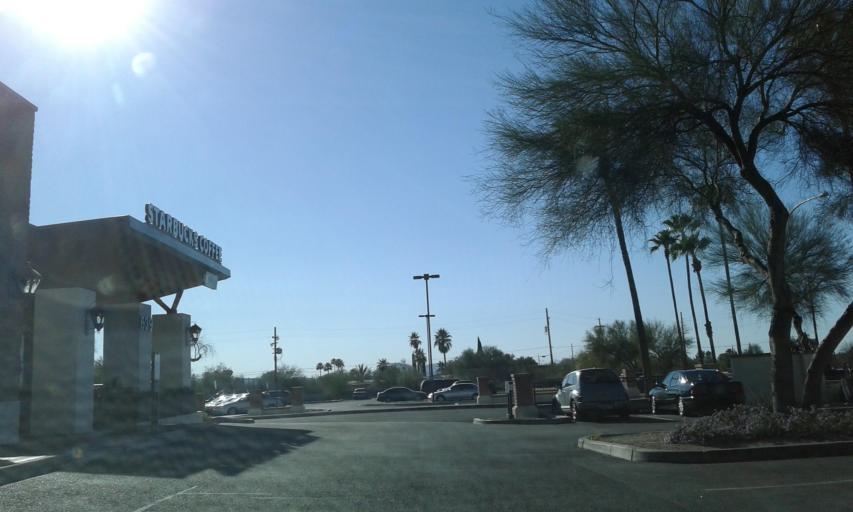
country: US
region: Arizona
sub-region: Pima County
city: Casas Adobes
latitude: 32.3368
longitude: -110.9790
